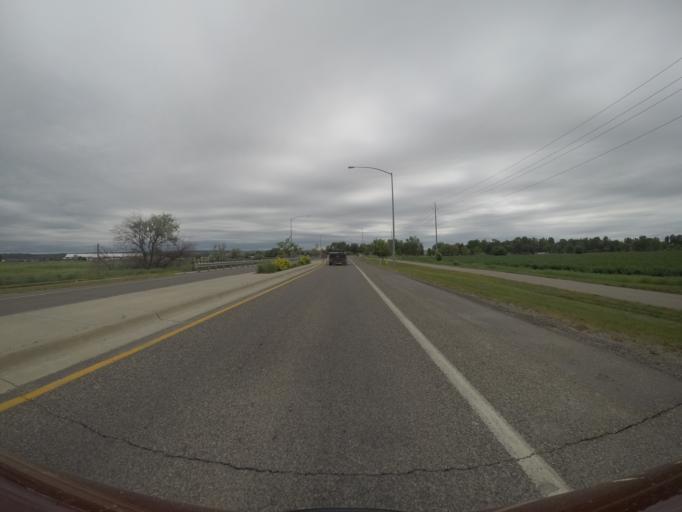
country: US
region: Montana
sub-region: Yellowstone County
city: Billings
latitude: 45.7347
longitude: -108.6175
